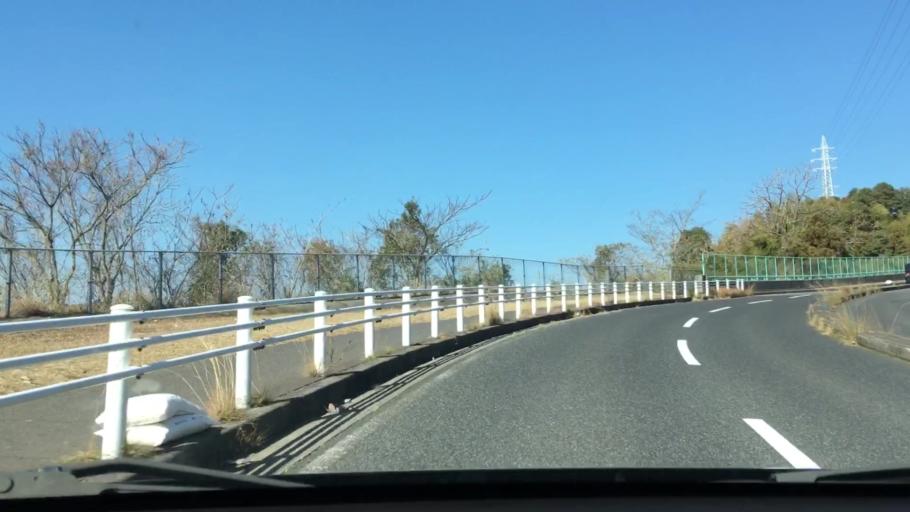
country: JP
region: Kagoshima
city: Kagoshima-shi
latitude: 31.5559
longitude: 130.5265
